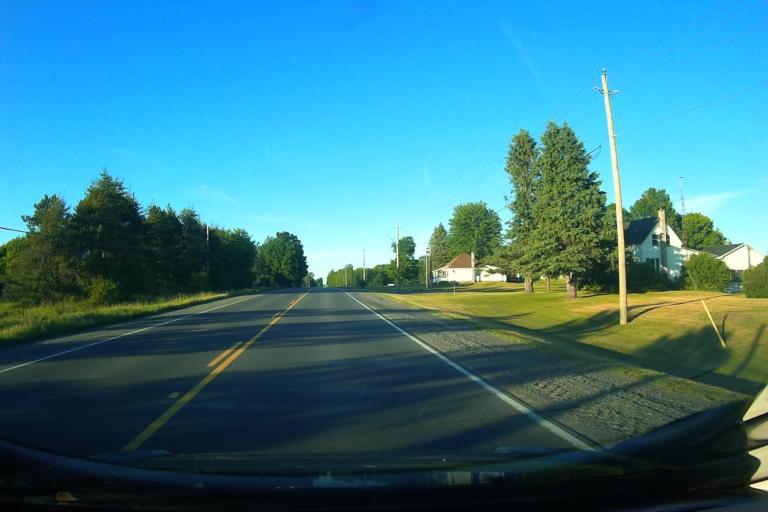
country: CA
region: Ontario
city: Prescott
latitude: 45.0084
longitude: -75.6779
